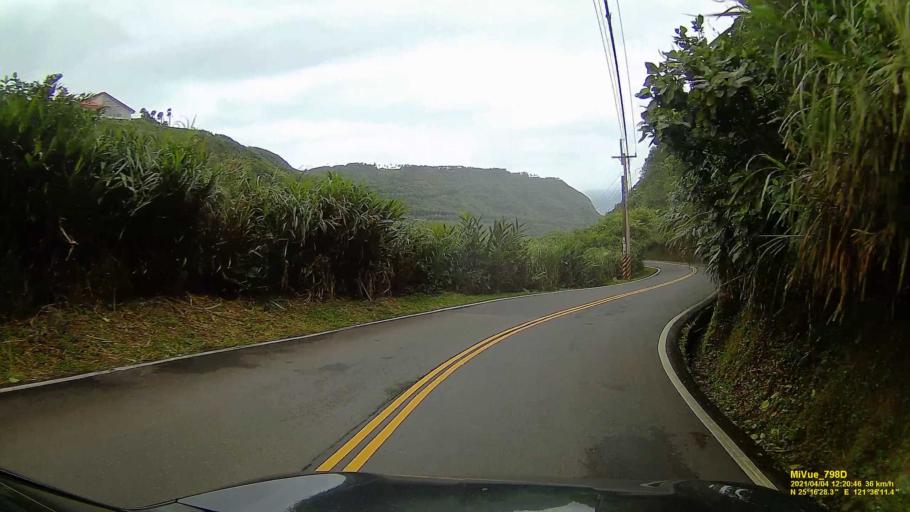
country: TW
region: Taiwan
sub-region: Keelung
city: Keelung
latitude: 25.2748
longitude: 121.6032
